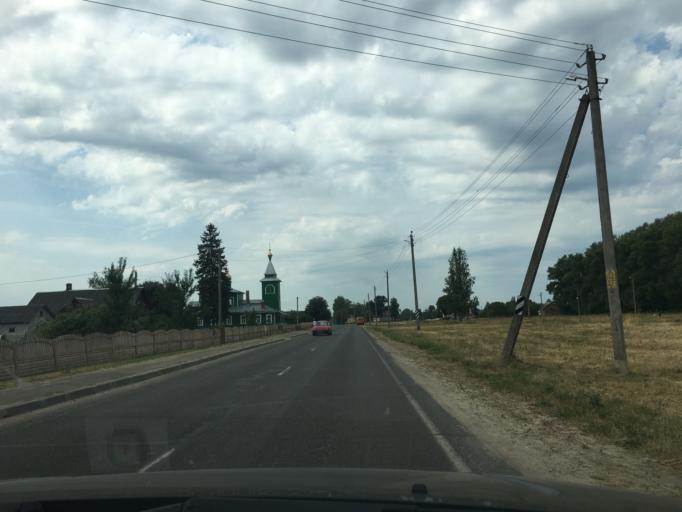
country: LT
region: Alytaus apskritis
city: Druskininkai
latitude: 53.8902
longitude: 24.1398
